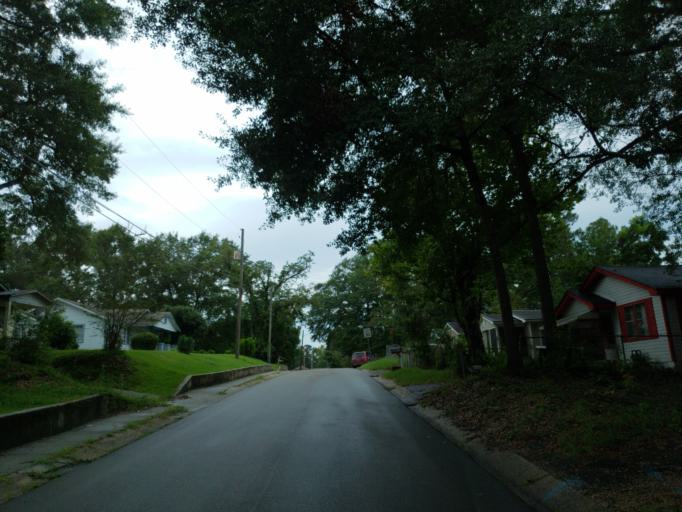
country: US
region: Mississippi
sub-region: Forrest County
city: Hattiesburg
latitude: 31.3102
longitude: -89.2965
